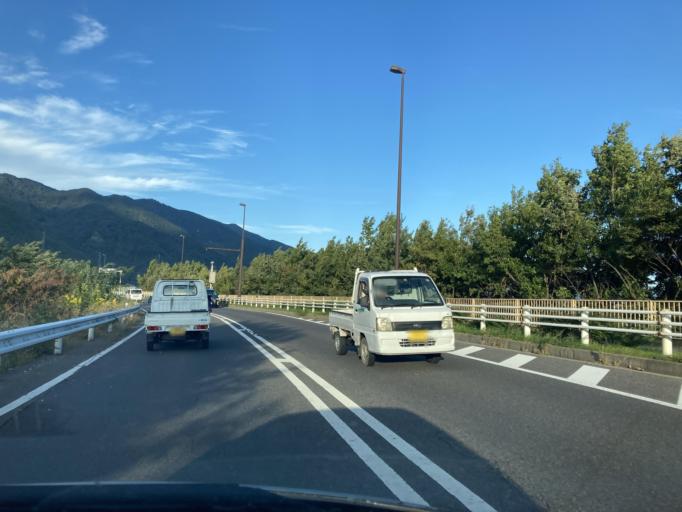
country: JP
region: Nagano
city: Ueda
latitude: 36.4055
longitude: 138.2128
